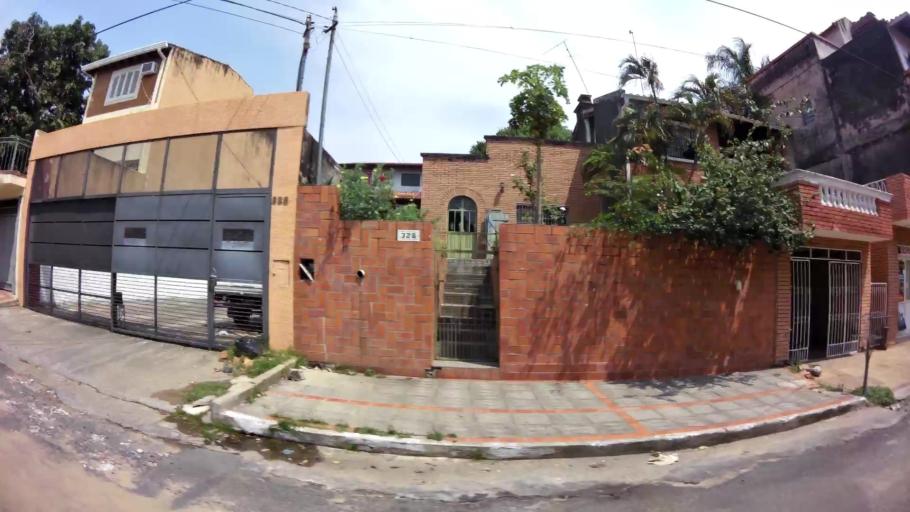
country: PY
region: Asuncion
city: Asuncion
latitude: -25.2782
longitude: -57.6083
